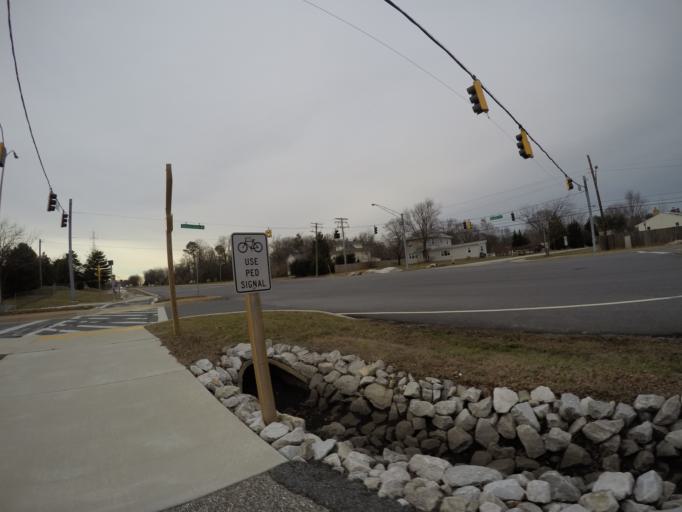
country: US
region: Maryland
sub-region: Anne Arundel County
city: Ferndale
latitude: 39.1797
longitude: -76.6509
